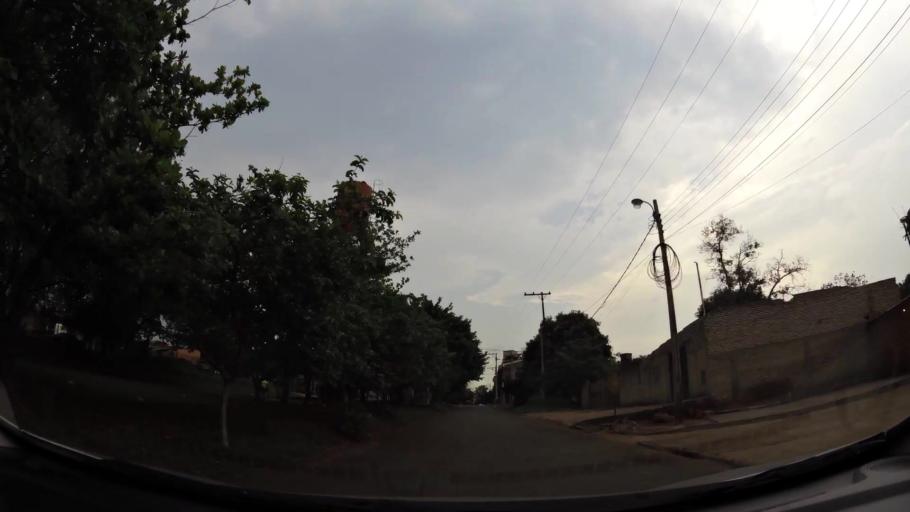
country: BR
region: Parana
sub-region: Foz Do Iguacu
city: Foz do Iguacu
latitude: -25.5435
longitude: -54.6002
